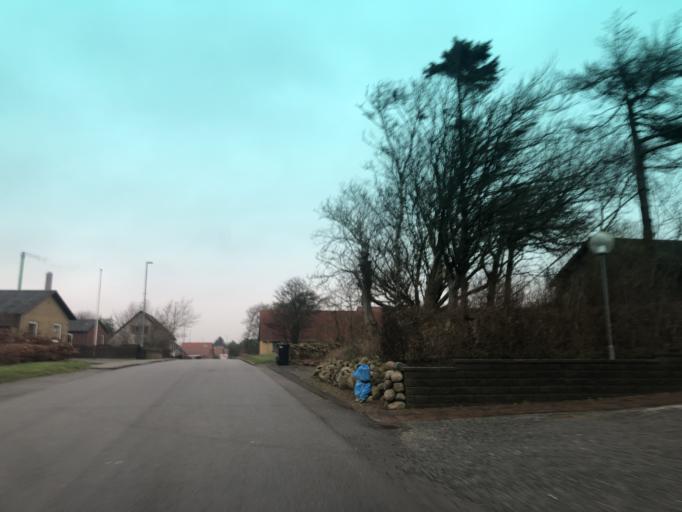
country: DK
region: North Denmark
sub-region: Thisted Kommune
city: Hurup
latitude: 56.7453
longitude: 8.4189
